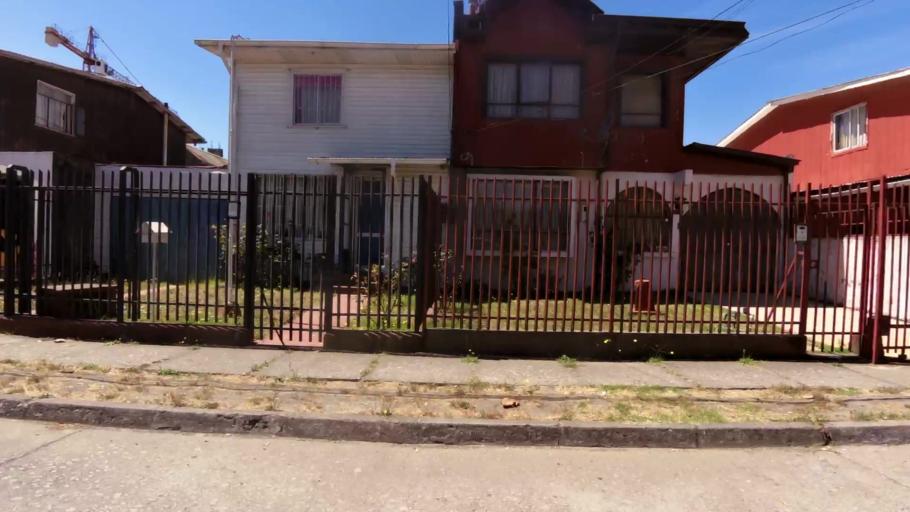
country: CL
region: Biobio
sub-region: Provincia de Concepcion
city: Talcahuano
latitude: -36.7635
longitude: -73.0858
